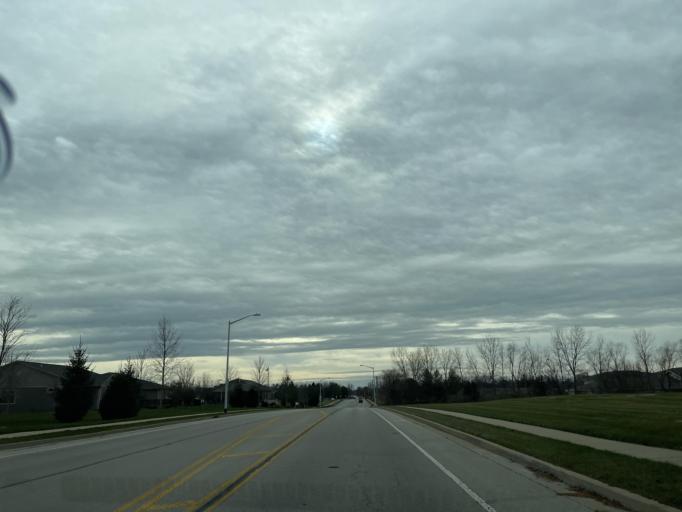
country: US
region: Illinois
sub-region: Sangamon County
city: Jerome
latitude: 39.7748
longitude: -89.7299
